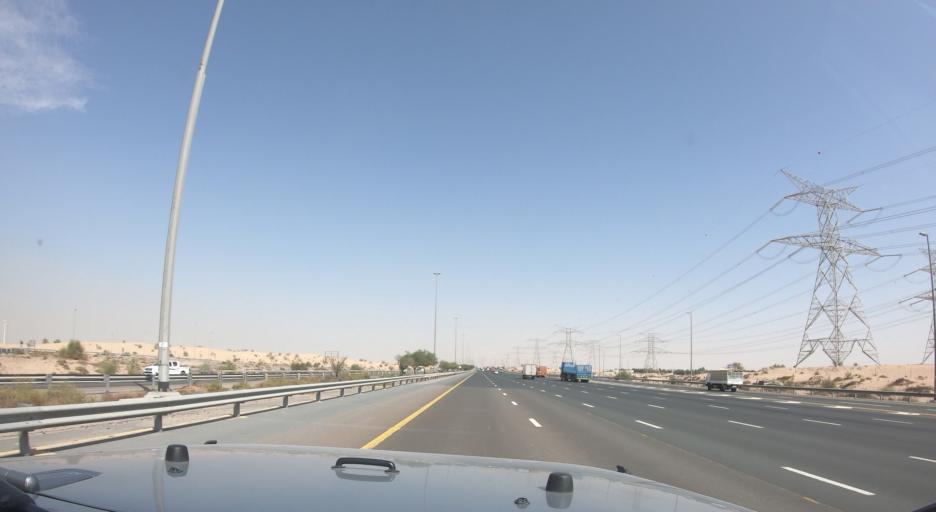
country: AE
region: Ash Shariqah
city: Sharjah
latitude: 25.1894
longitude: 55.5305
